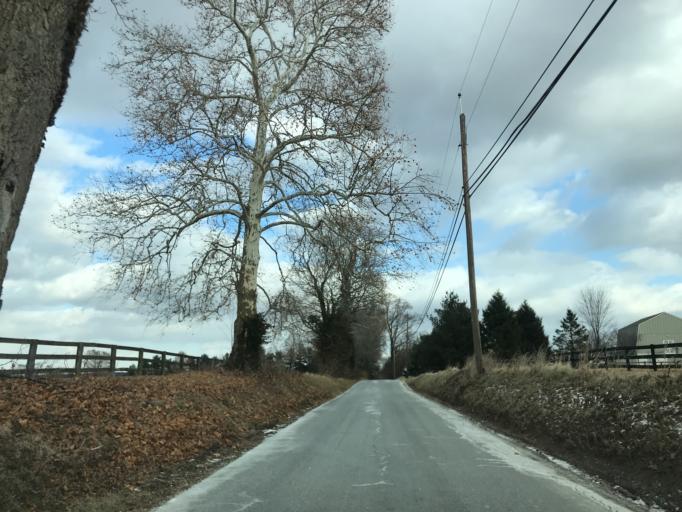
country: US
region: Maryland
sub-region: Harford County
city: Jarrettsville
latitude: 39.5749
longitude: -76.5671
